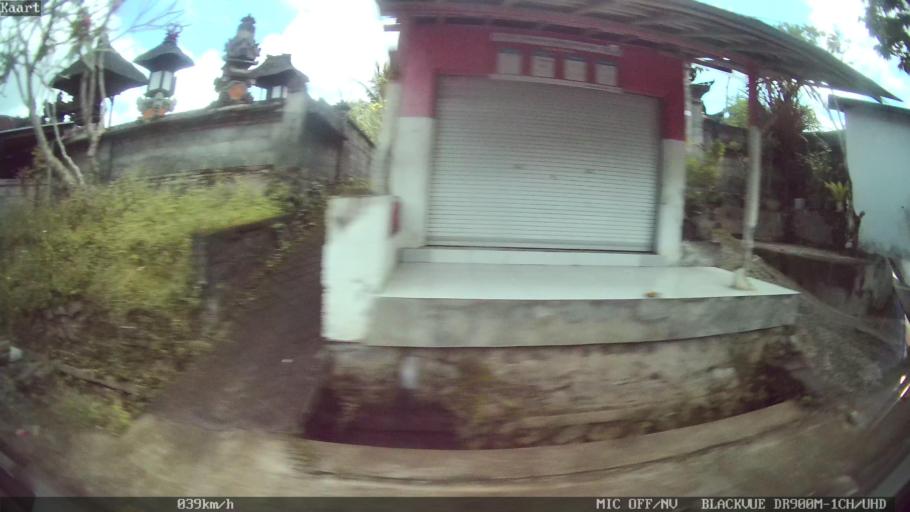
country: ID
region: Bali
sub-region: Kabupaten Gianyar
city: Ubud
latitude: -8.5417
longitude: 115.2802
